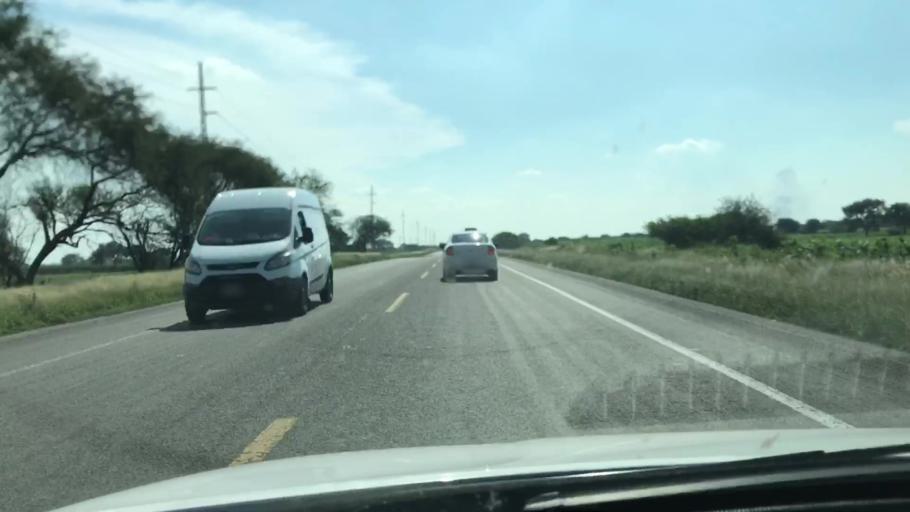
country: MX
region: Michoacan
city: Vistahermosa de Negrete
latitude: 20.2716
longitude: -102.4230
